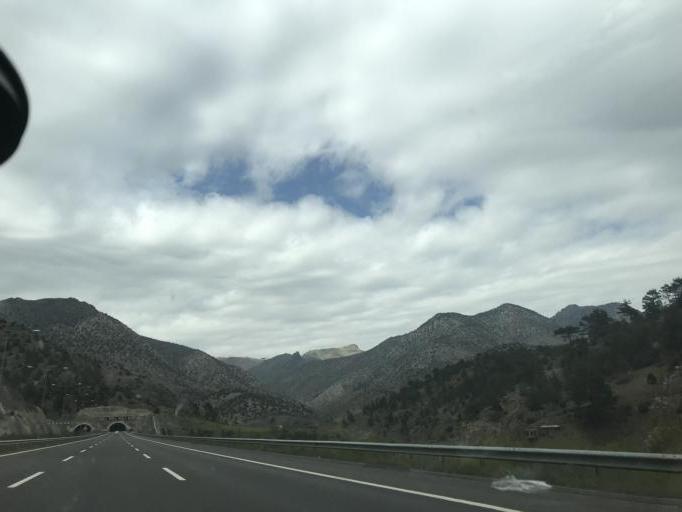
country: TR
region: Nigde
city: Ciftehan
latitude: 37.5163
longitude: 34.8177
